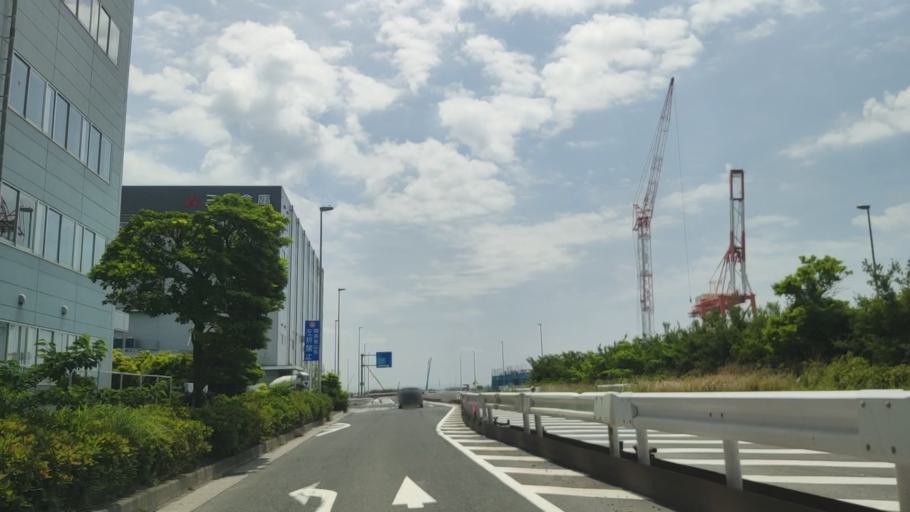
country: JP
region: Kanagawa
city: Yokohama
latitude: 35.4062
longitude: 139.6834
